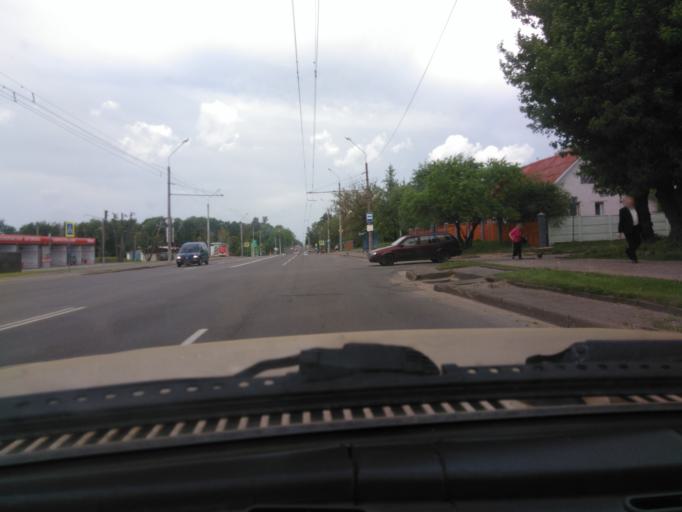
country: BY
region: Mogilev
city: Mahilyow
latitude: 53.9333
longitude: 30.3359
